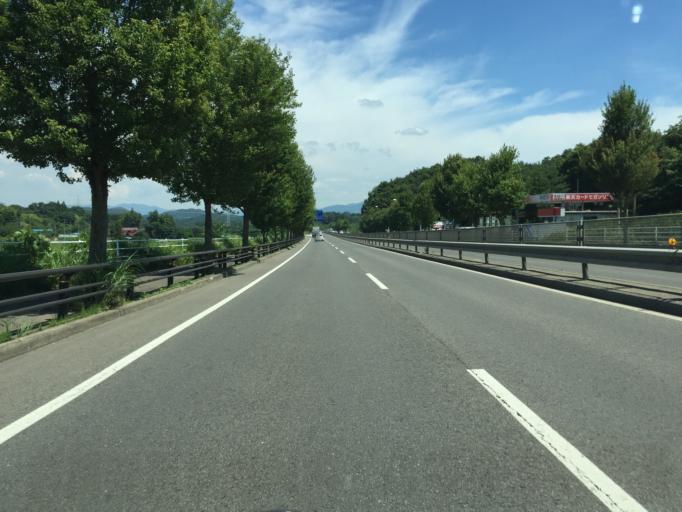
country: JP
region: Fukushima
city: Fukushima-shi
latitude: 37.6864
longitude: 140.4668
